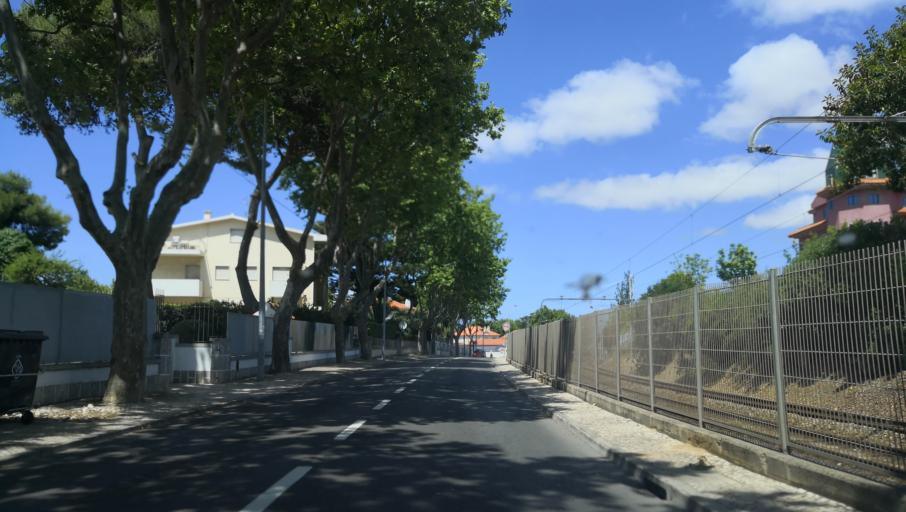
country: PT
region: Lisbon
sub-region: Cascais
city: Parede
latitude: 38.6875
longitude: -9.3501
